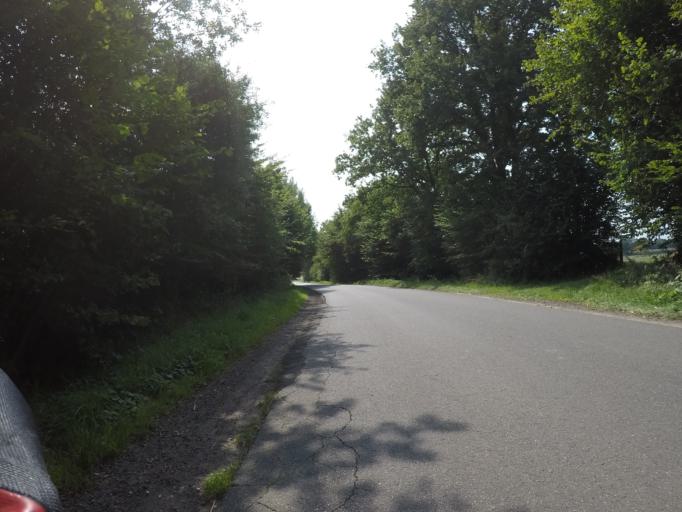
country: DE
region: Schleswig-Holstein
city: Henstedt-Ulzburg
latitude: 53.7722
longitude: 10.0190
